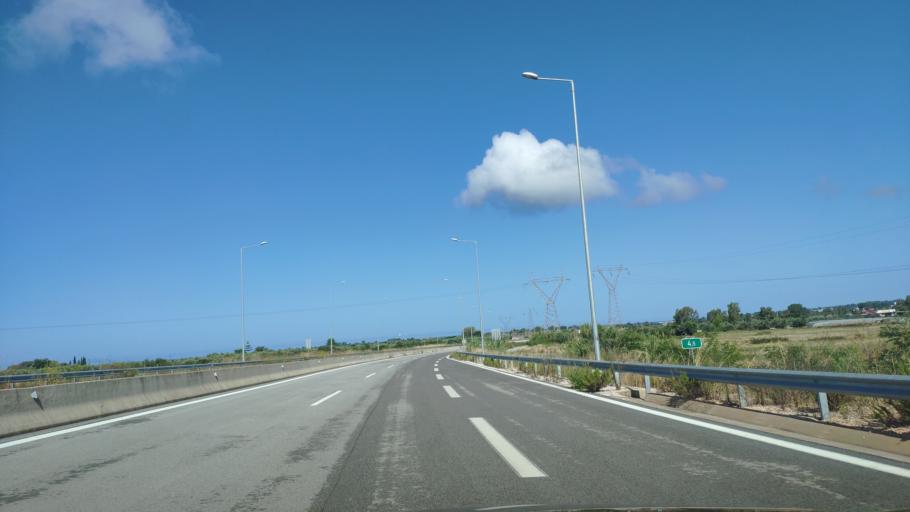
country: GR
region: Epirus
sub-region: Nomos Prevezis
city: Preveza
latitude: 38.9127
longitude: 20.8003
